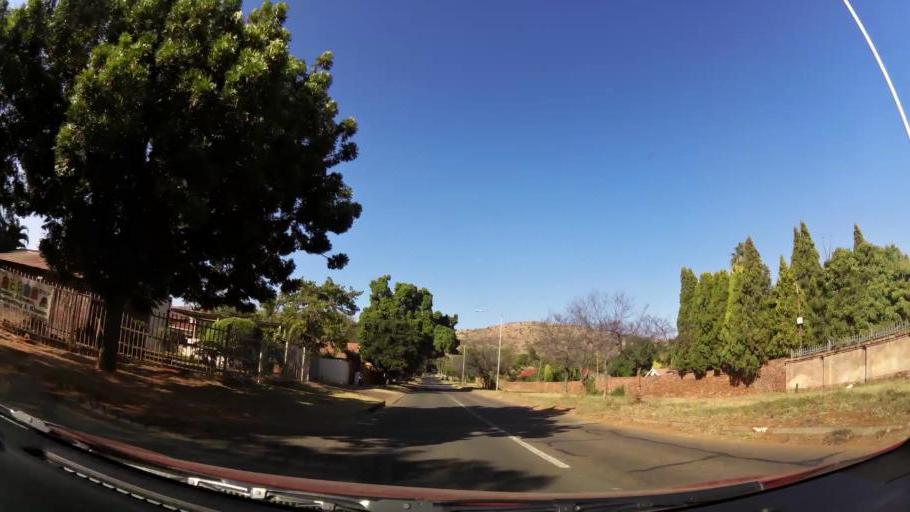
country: ZA
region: Gauteng
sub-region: City of Tshwane Metropolitan Municipality
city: Pretoria
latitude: -25.6790
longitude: 28.1434
